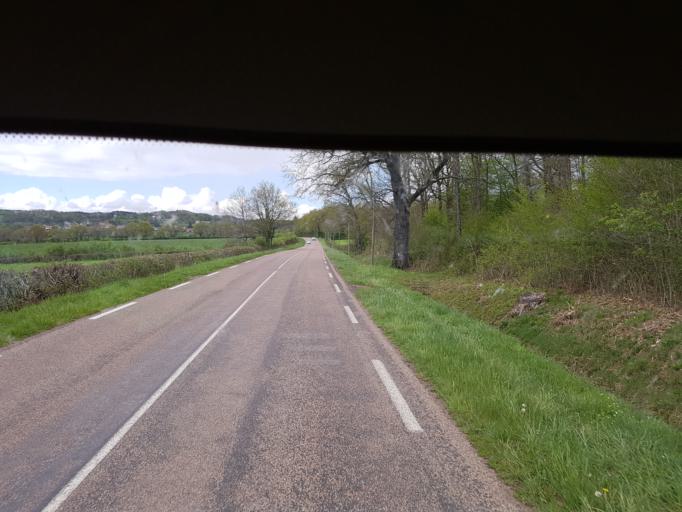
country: FR
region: Bourgogne
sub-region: Departement de Saone-et-Loire
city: Autun
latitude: 47.0300
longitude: 4.2831
